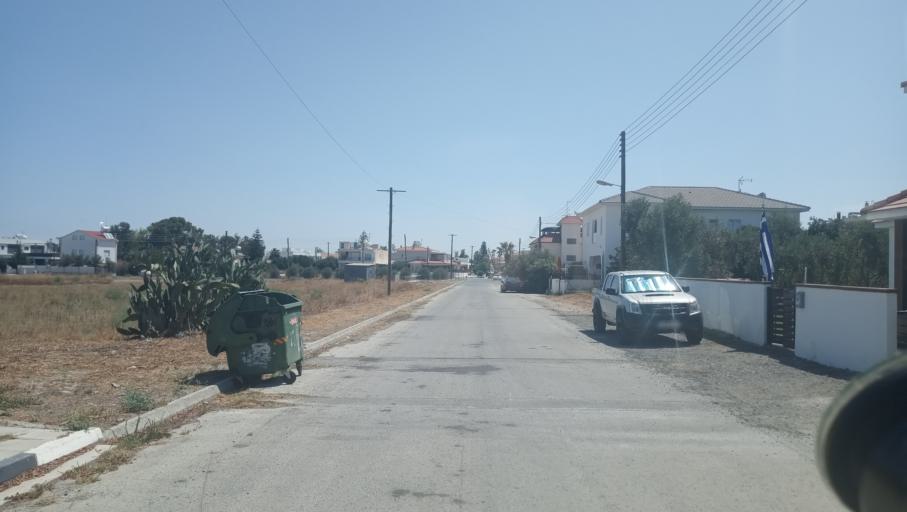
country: CY
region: Lefkosia
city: Psimolofou
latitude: 35.0617
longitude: 33.2614
